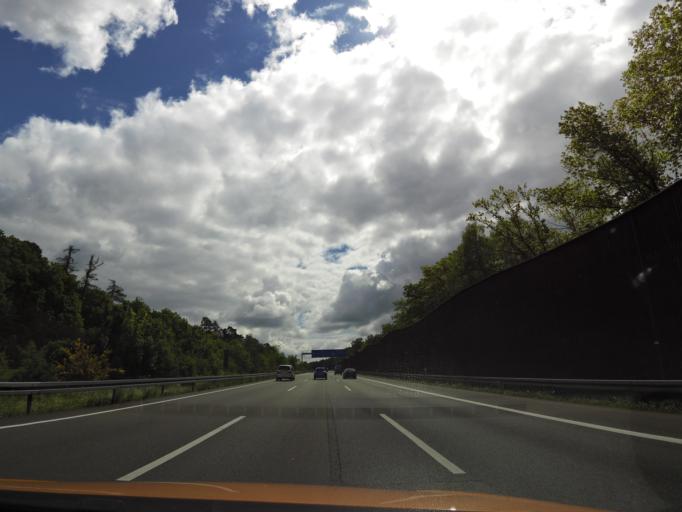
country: DE
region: Lower Saxony
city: Helmstedt
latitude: 52.2495
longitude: 11.0009
